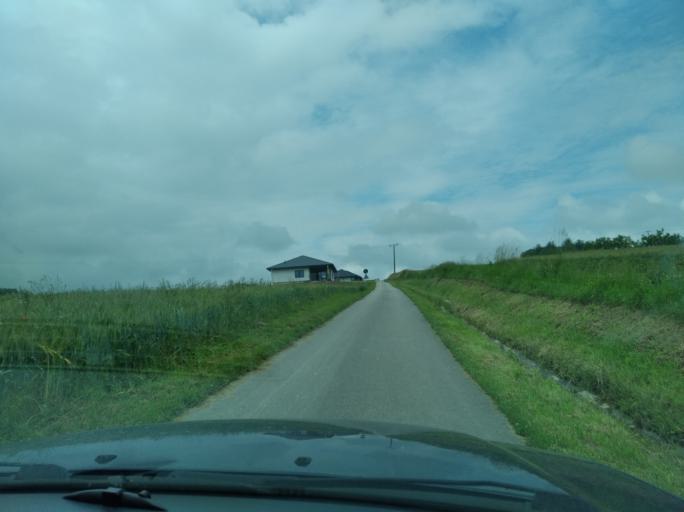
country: PL
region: Subcarpathian Voivodeship
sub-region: Powiat jaroslawski
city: Pruchnik
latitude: 49.9005
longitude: 22.5020
